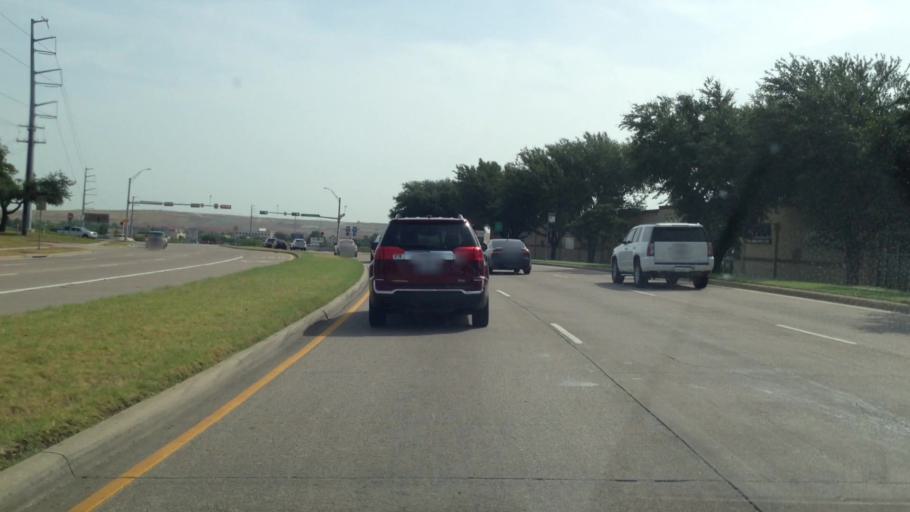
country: US
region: Texas
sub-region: Denton County
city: Lewisville
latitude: 33.0054
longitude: -96.9735
